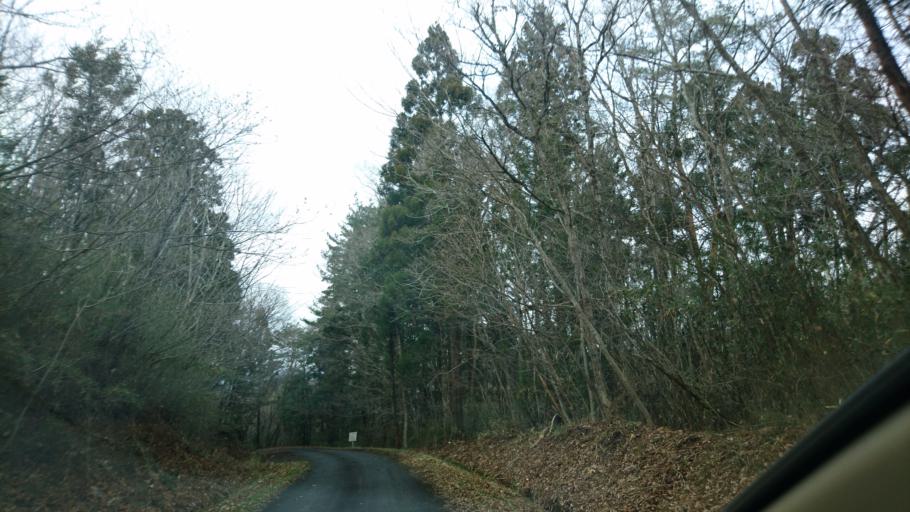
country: JP
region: Iwate
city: Ichinoseki
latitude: 38.8956
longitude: 141.1618
